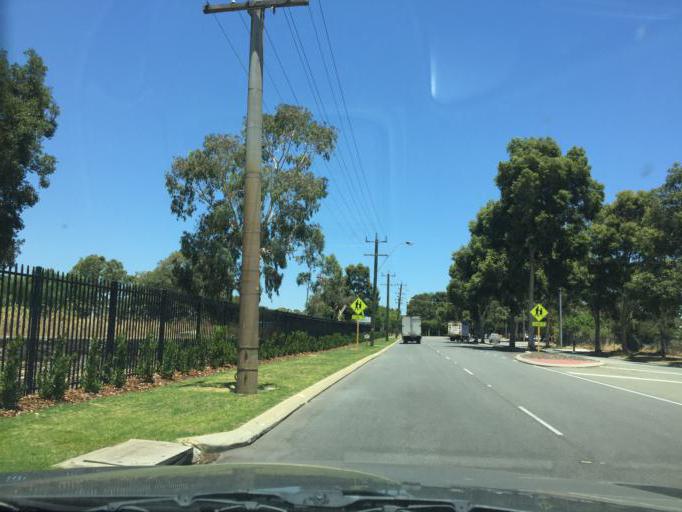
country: AU
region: Western Australia
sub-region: Canning
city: Canning Vale
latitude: -32.0615
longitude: 115.9294
